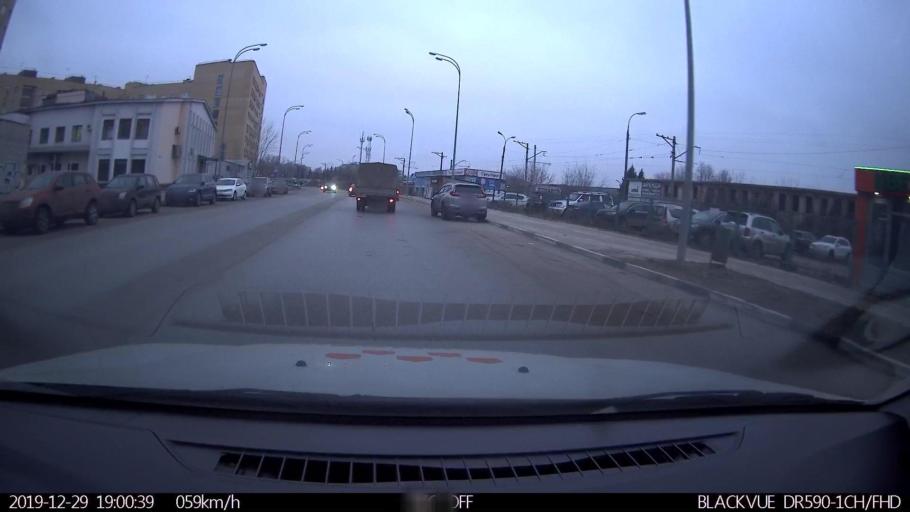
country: RU
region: Nizjnij Novgorod
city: Neklyudovo
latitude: 56.3537
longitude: 43.8699
